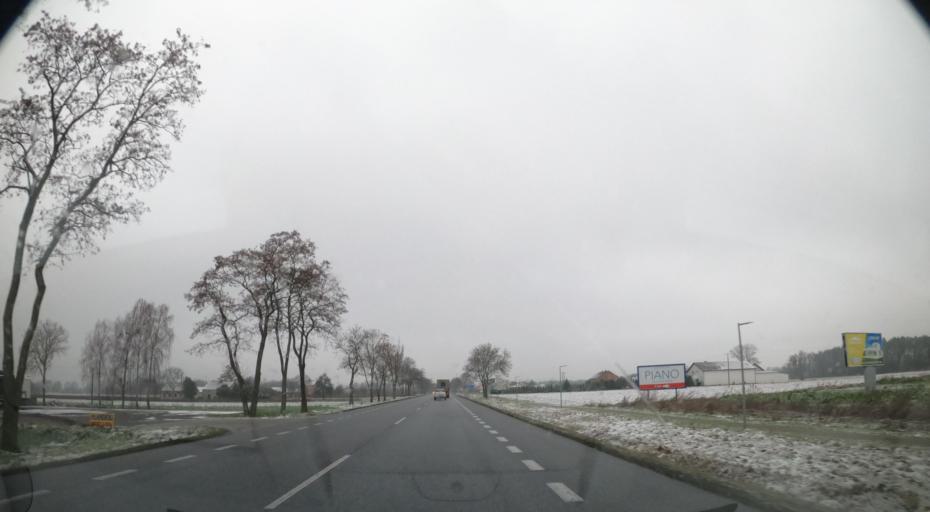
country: PL
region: Masovian Voivodeship
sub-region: Powiat sochaczewski
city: Sochaczew
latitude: 52.2218
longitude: 20.3226
